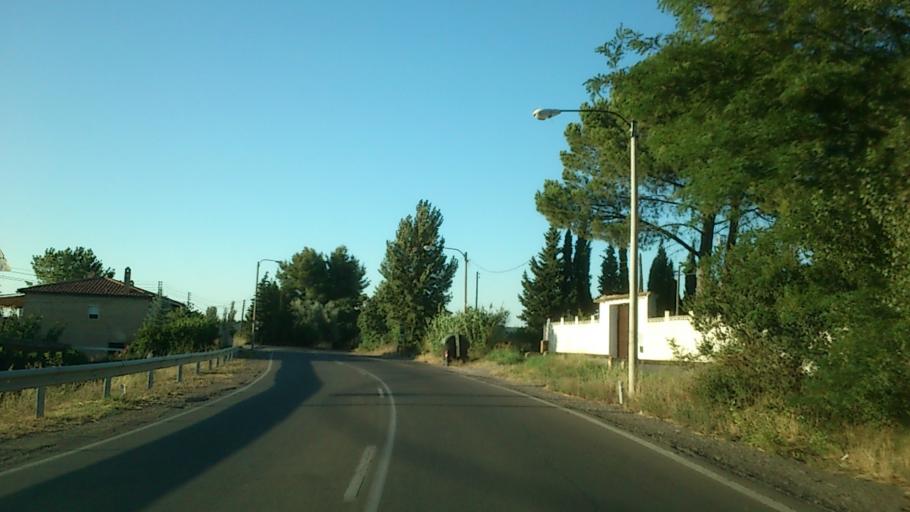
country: ES
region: Aragon
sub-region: Provincia de Zaragoza
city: Villanueva de Gallego
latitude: 41.7148
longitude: -0.8109
